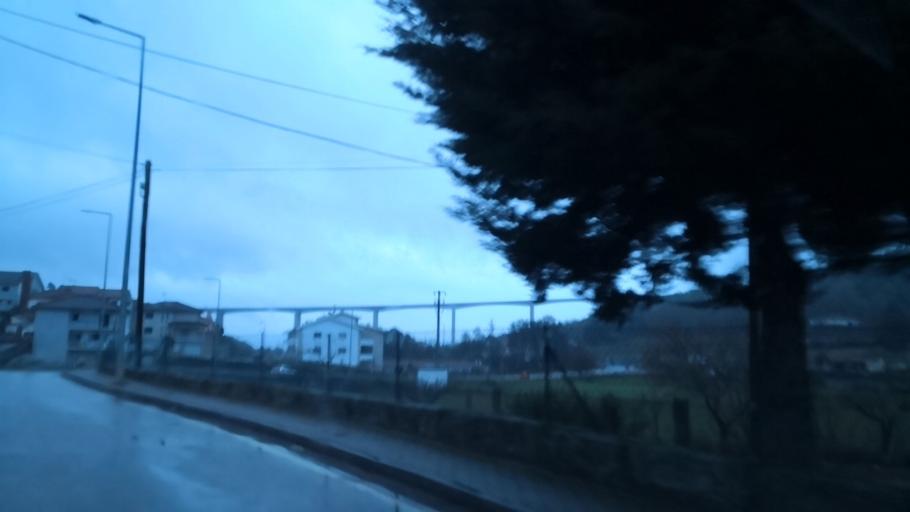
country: PT
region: Vila Real
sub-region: Vila Pouca de Aguiar
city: Vila Pouca de Aguiar
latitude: 41.4918
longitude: -7.6462
